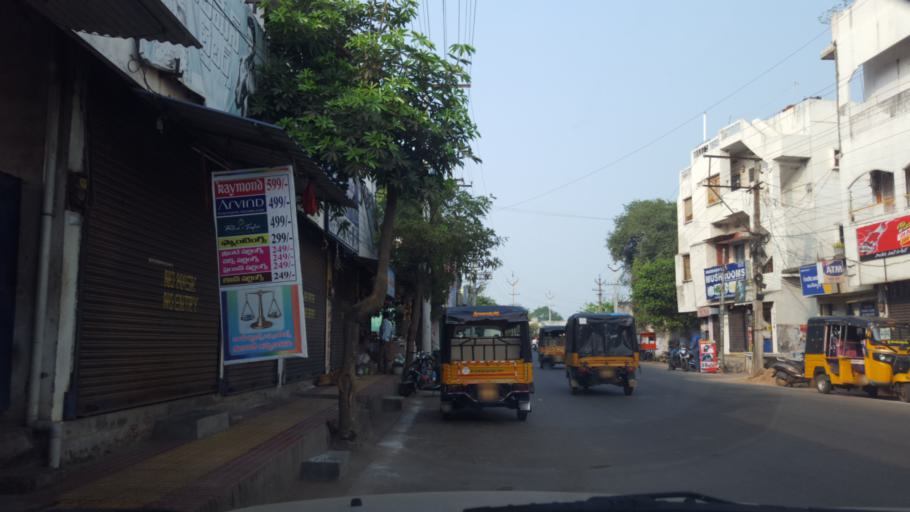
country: IN
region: Andhra Pradesh
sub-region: Srikakulam
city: Srikakulam
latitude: 18.2895
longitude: 83.8962
